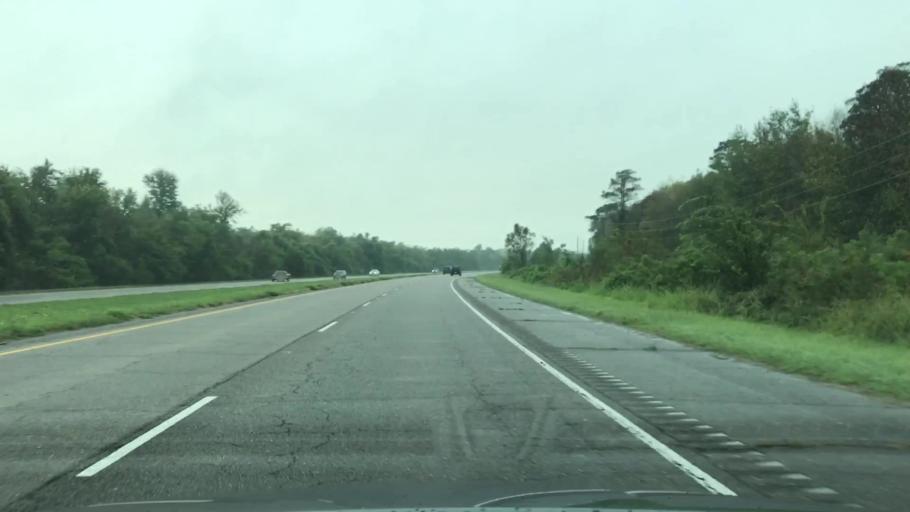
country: US
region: Louisiana
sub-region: Lafourche Parish
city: Raceland
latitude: 29.7234
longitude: -90.5599
